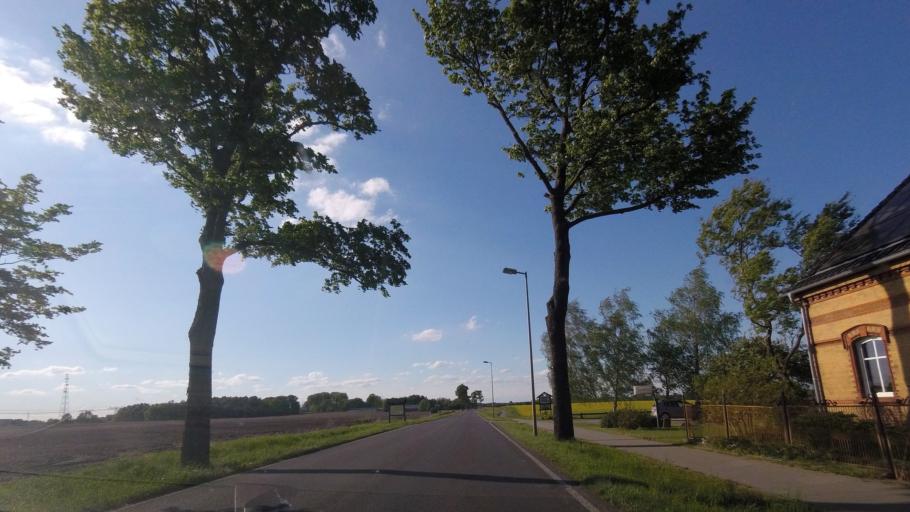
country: DE
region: Brandenburg
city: Lubbenau
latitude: 51.8707
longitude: 13.9162
